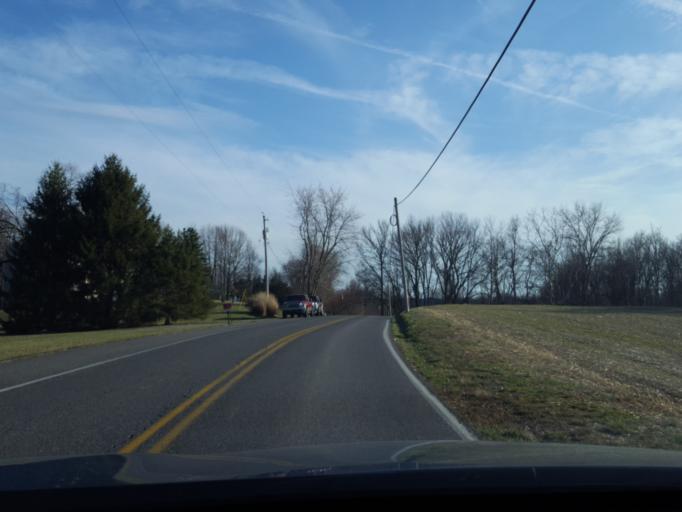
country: US
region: Maryland
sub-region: Anne Arundel County
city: Deale
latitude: 38.7771
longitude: -76.5748
